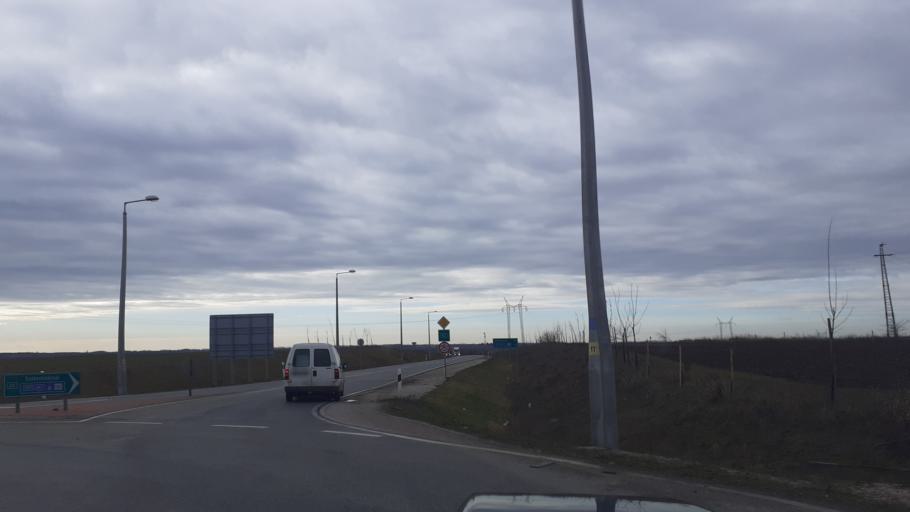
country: HU
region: Fejer
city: Seregelyes
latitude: 47.1054
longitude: 18.6282
